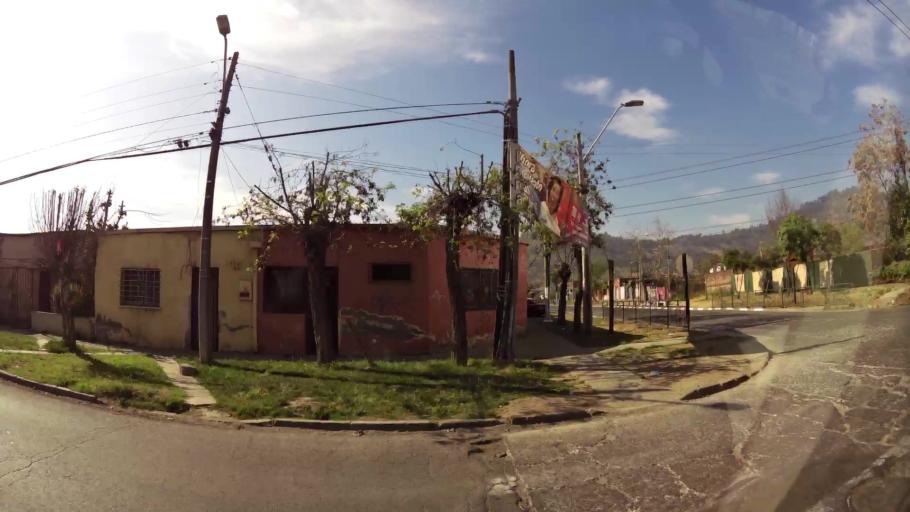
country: CL
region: Santiago Metropolitan
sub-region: Provincia de Santiago
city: Santiago
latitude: -33.4019
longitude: -70.6290
